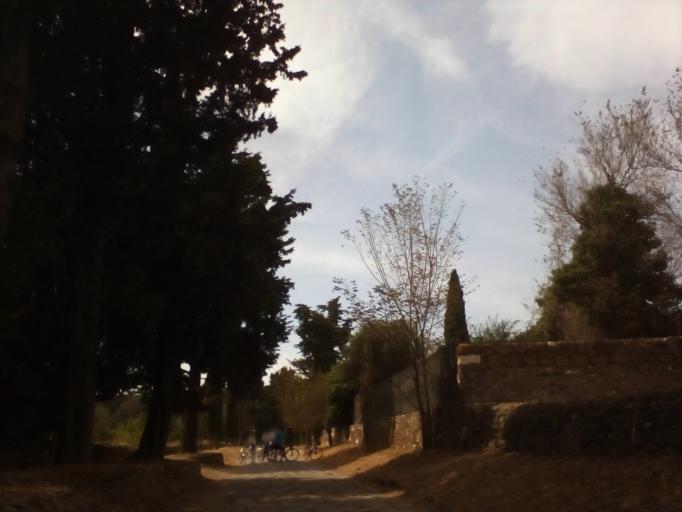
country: IT
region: Latium
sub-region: Citta metropolitana di Roma Capitale
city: Rome
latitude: 41.8459
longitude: 12.5278
